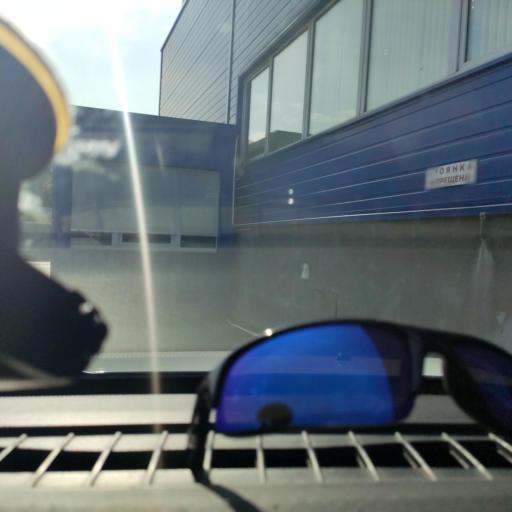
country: RU
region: Samara
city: Petra-Dubrava
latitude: 53.2780
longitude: 50.2783
